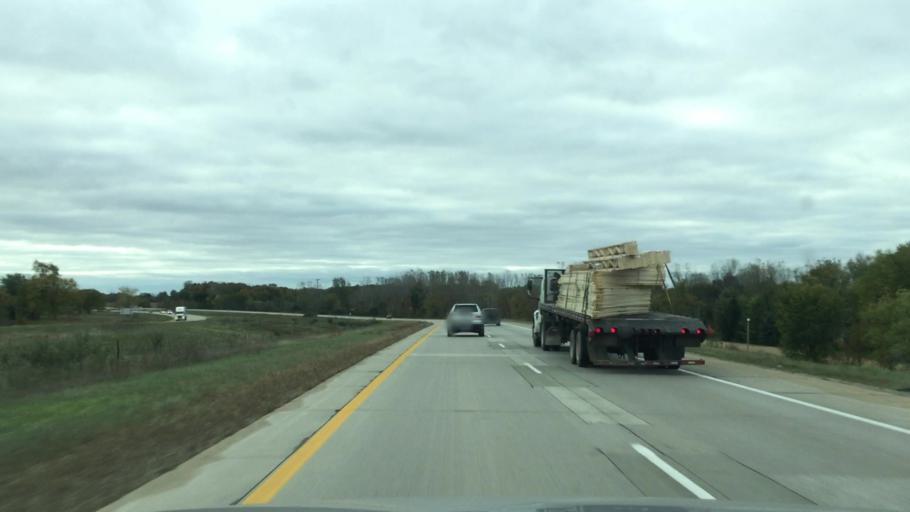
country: US
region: Michigan
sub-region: Lapeer County
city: Imlay City
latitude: 43.0020
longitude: -83.1481
